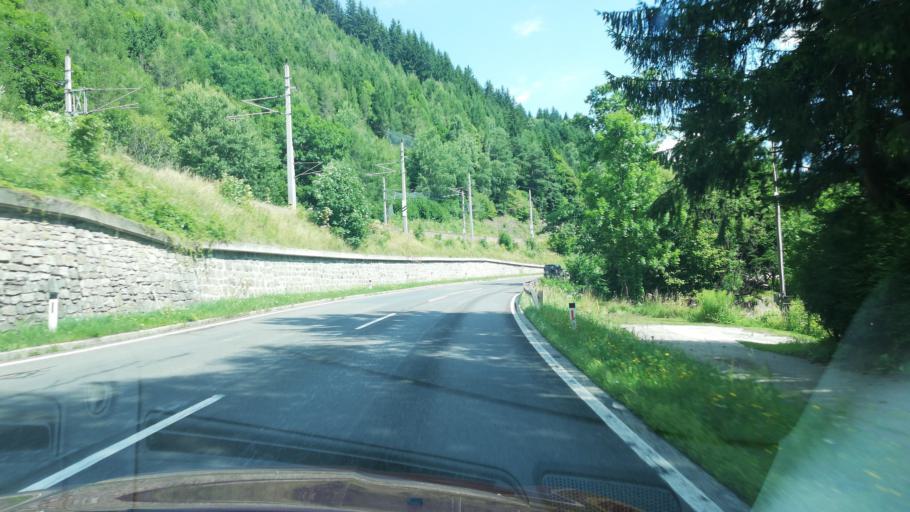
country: AT
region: Styria
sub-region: Politischer Bezirk Murau
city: Durnstein in der Steiermark
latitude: 47.0077
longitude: 14.3997
